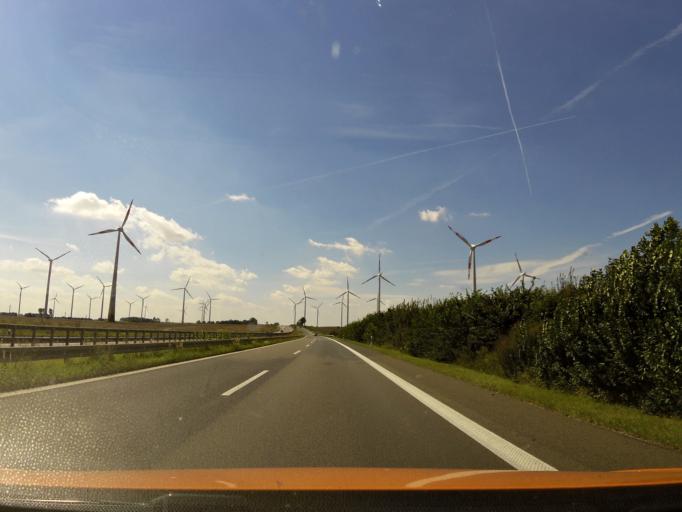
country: DE
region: Brandenburg
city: Gramzow
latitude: 53.2802
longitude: 14.0709
